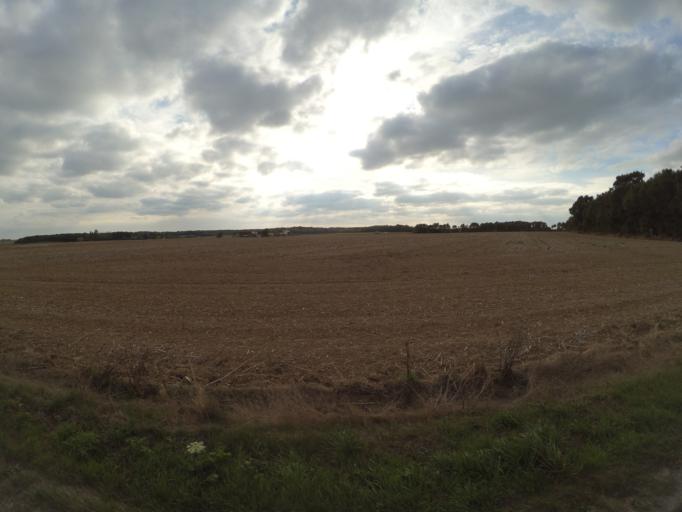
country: FR
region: Centre
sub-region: Departement d'Indre-et-Loire
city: Nazelles-Negron
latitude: 47.4799
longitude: 0.9548
